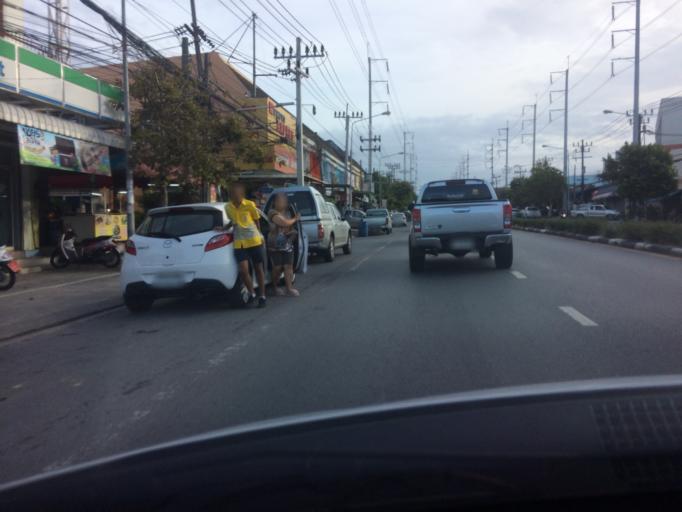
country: TH
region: Phuket
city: Mueang Phuket
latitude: 7.8623
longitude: 98.3804
